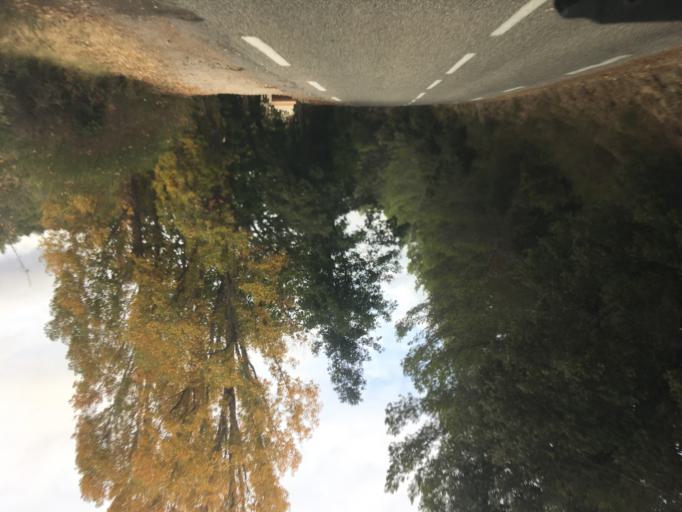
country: FR
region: Provence-Alpes-Cote d'Azur
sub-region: Departement du Var
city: Villecroze
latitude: 43.5917
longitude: 6.2794
